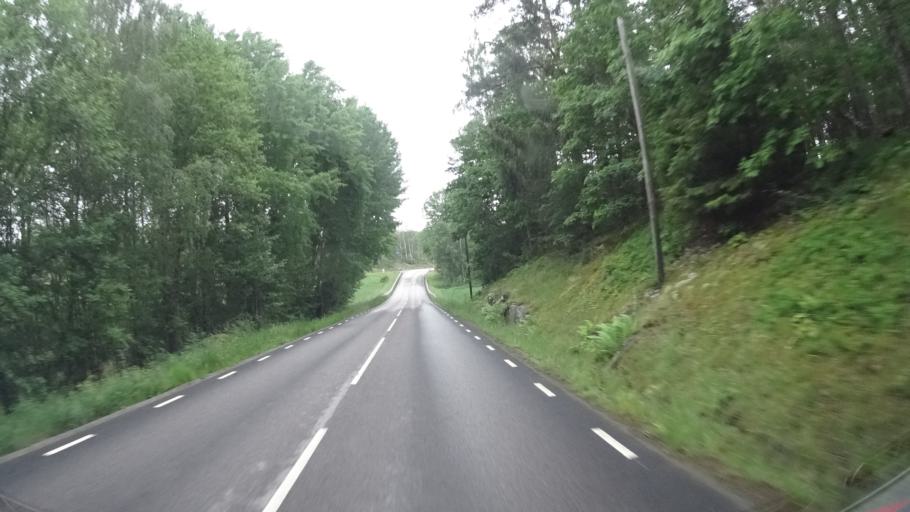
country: SE
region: Kalmar
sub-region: Oskarshamns Kommun
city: Oskarshamn
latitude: 57.3603
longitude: 16.2353
